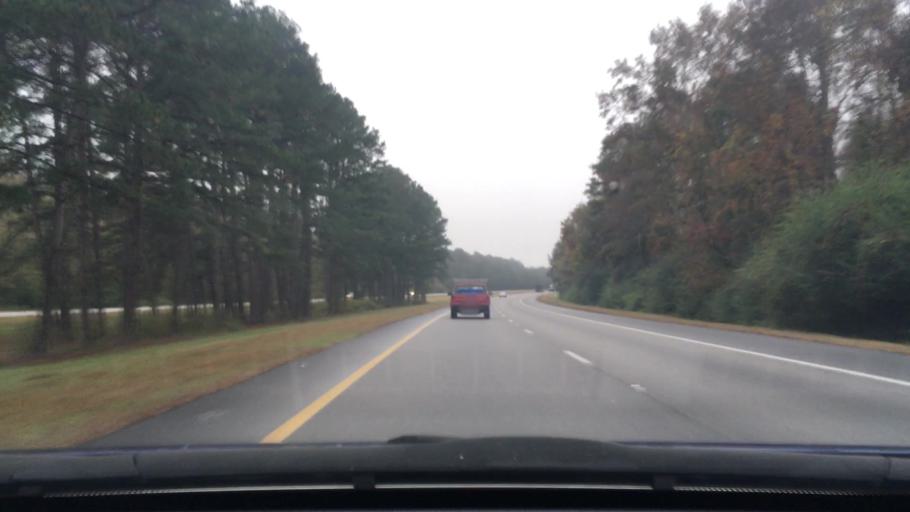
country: US
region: South Carolina
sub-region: Lee County
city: Bishopville
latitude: 34.1955
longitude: -80.3305
